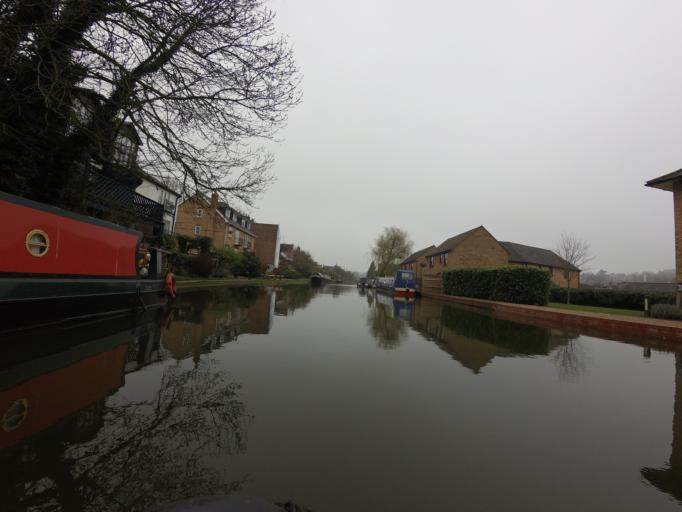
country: GB
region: England
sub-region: Hertfordshire
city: Berkhamsted
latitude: 51.7620
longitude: -0.5591
